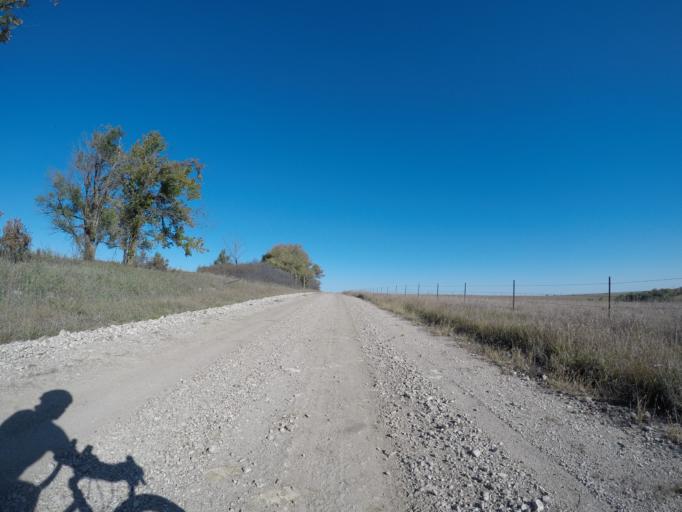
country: US
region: Kansas
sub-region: Wabaunsee County
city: Alma
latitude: 38.8753
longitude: -96.4096
